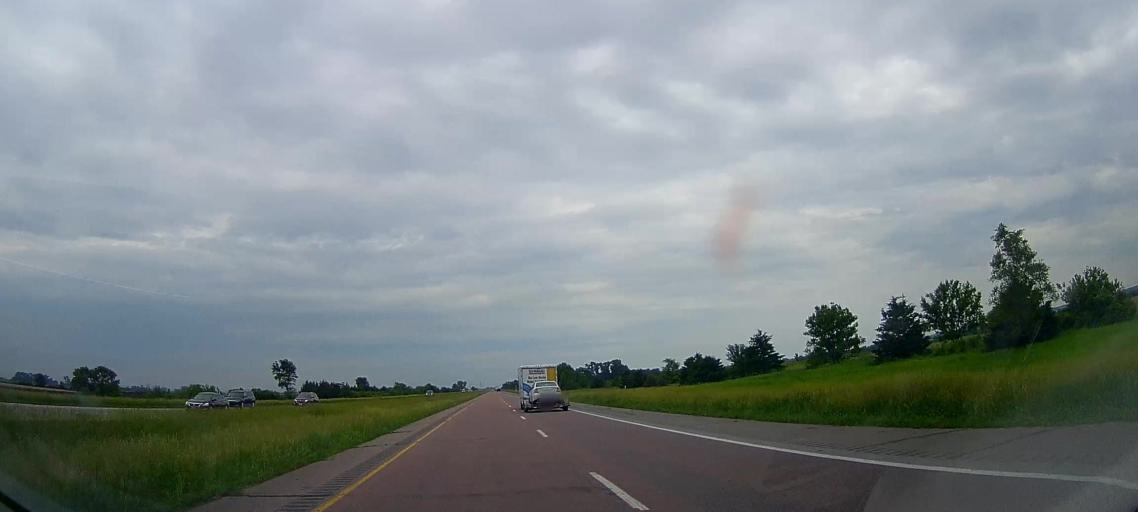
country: US
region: Iowa
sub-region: Woodbury County
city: Sergeant Bluff
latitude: 42.3508
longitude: -96.3349
